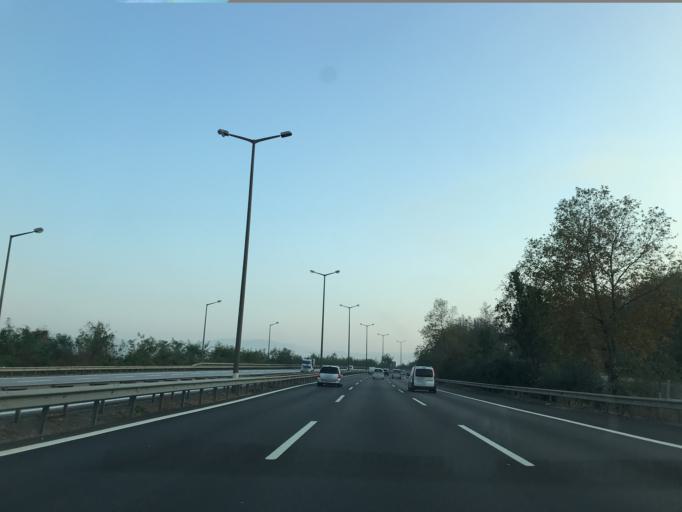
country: TR
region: Sakarya
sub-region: Merkez
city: Sapanca
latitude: 40.6935
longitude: 30.2860
